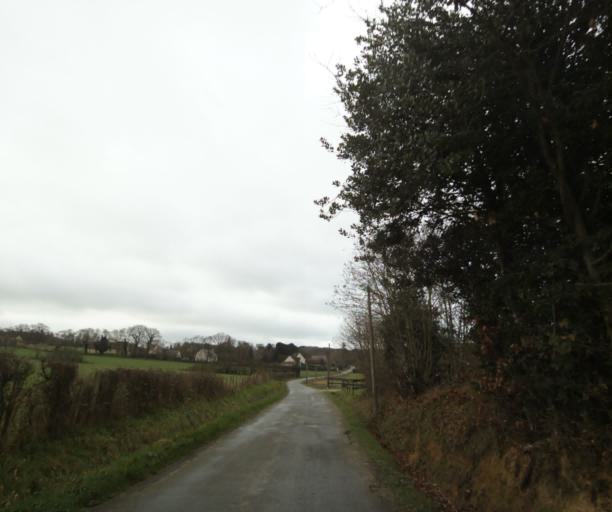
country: FR
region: Pays de la Loire
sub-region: Departement de la Sarthe
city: La Chapelle-Saint-Aubin
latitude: 48.0293
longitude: 0.1469
